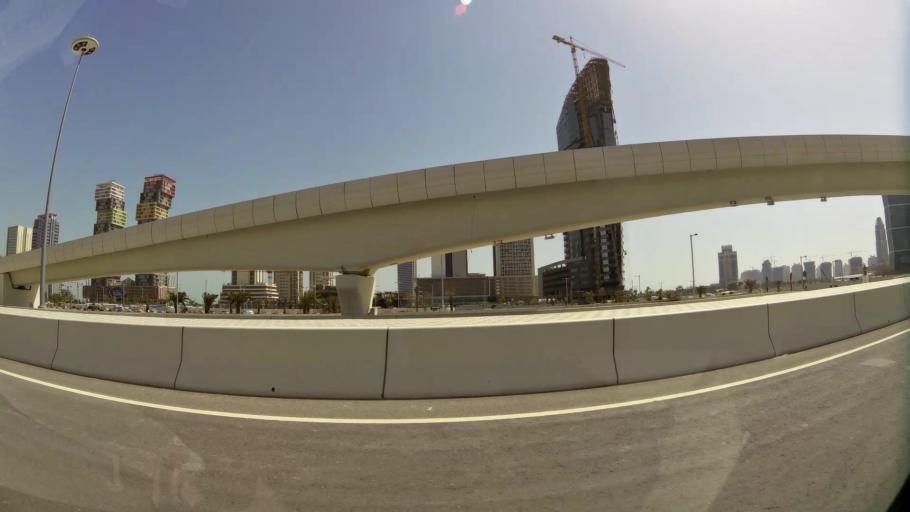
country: QA
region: Baladiyat ad Dawhah
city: Doha
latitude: 25.3831
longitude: 51.5206
